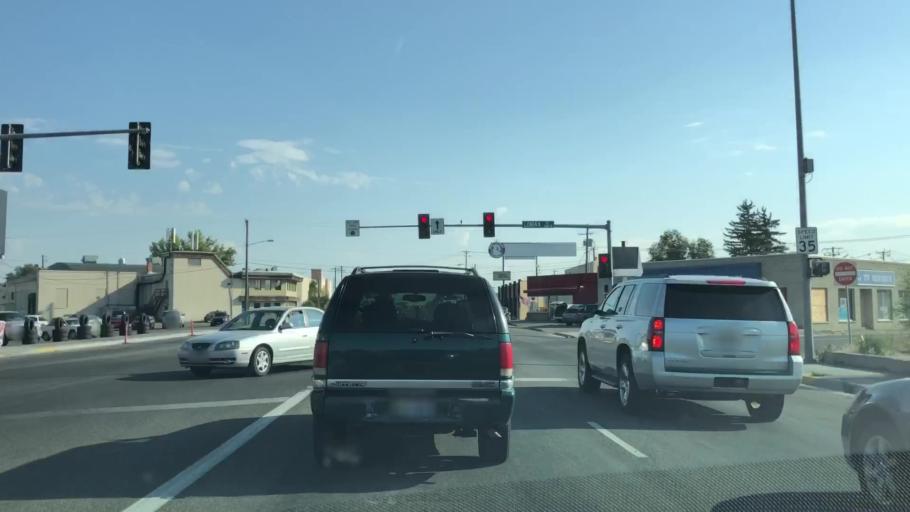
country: US
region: Idaho
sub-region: Bonneville County
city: Idaho Falls
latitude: 43.4977
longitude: -112.0326
